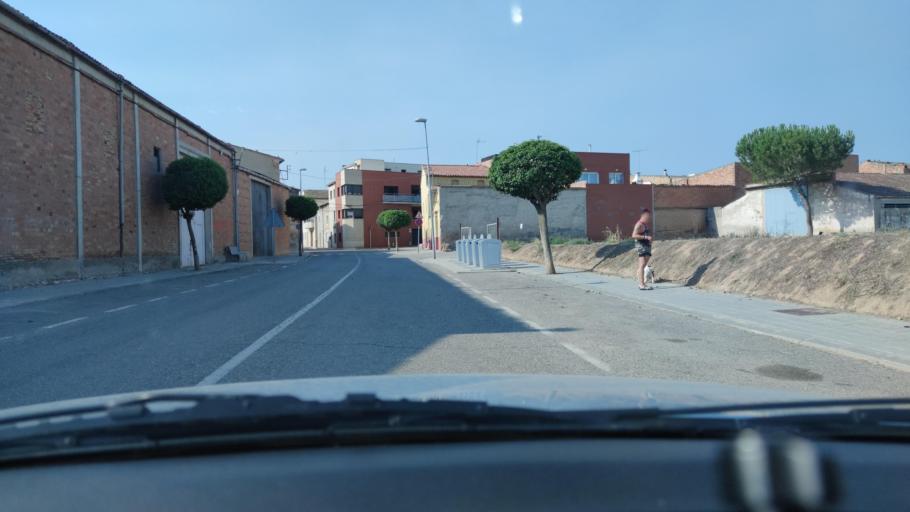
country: ES
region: Catalonia
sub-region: Provincia de Lleida
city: Juneda
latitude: 41.5830
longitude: 0.8339
